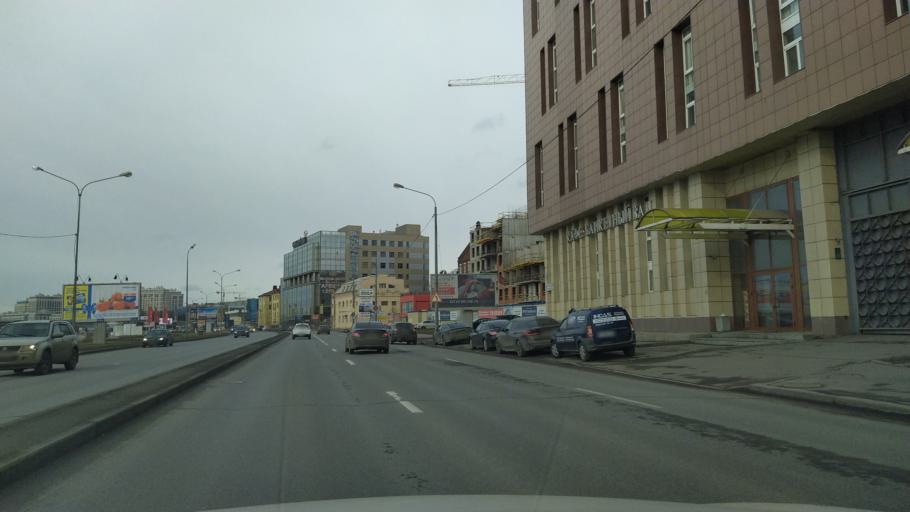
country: RU
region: Leningrad
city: Sampsonievskiy
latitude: 59.9755
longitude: 30.3309
